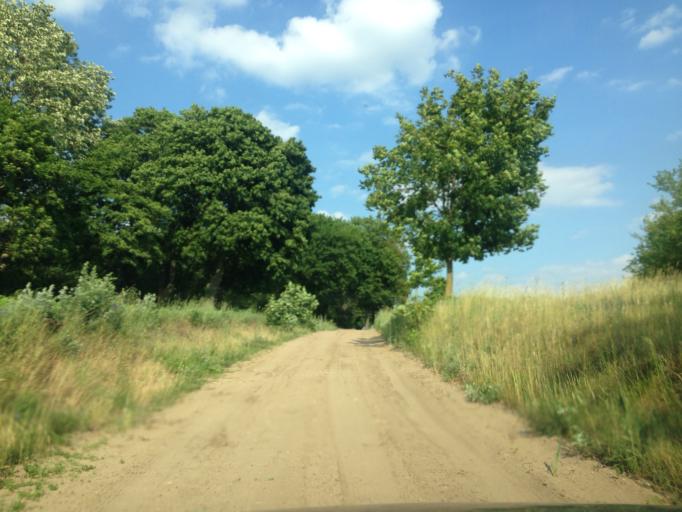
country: PL
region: Kujawsko-Pomorskie
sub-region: Powiat brodnicki
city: Brzozie
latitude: 53.2898
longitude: 19.6851
